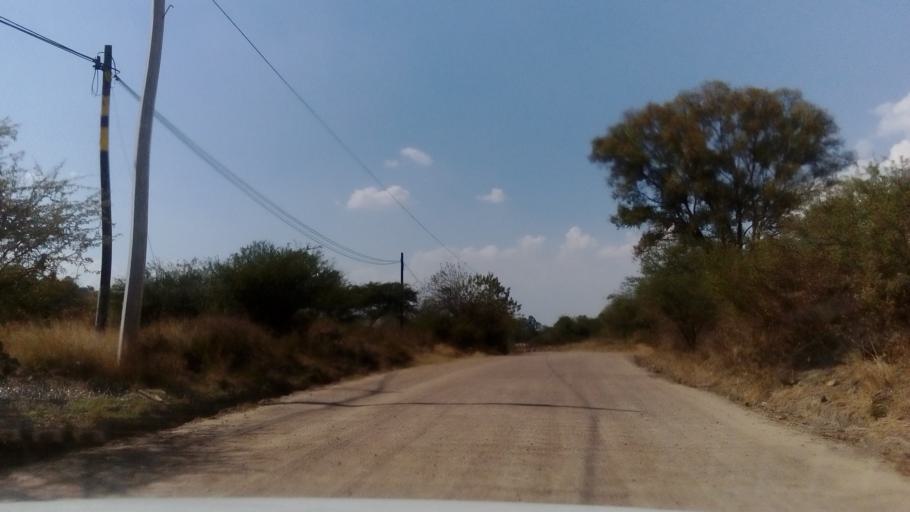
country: MX
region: Guanajuato
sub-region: Silao de la Victoria
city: San Francisco (Banos de Agua Caliente)
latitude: 21.0769
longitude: -101.4919
